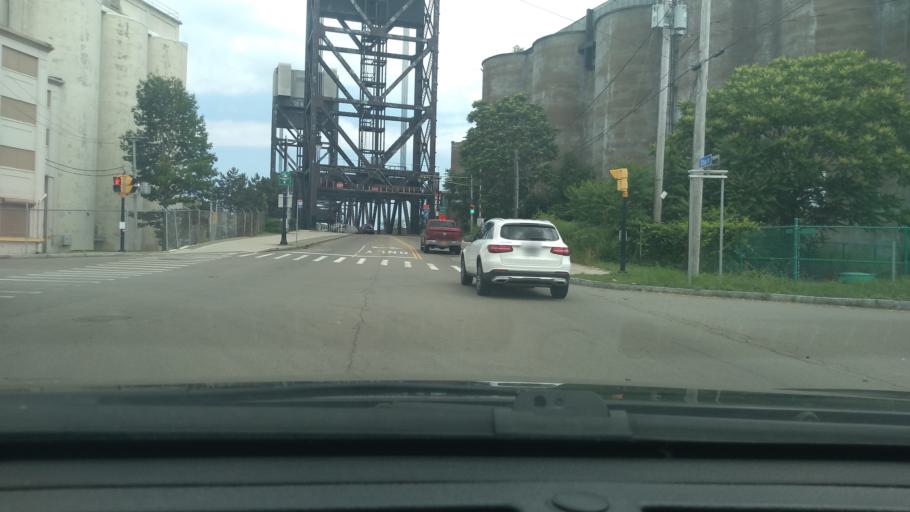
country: US
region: New York
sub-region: Erie County
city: Buffalo
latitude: 42.8606
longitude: -78.8676
